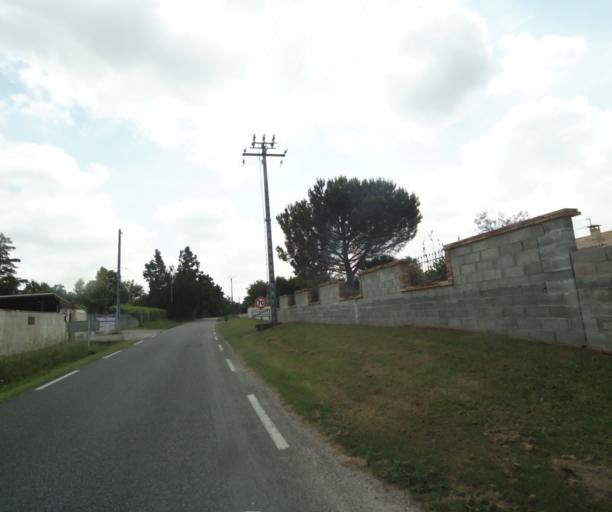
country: FR
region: Midi-Pyrenees
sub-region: Departement du Tarn-et-Garonne
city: Albias
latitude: 44.0566
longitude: 1.3987
